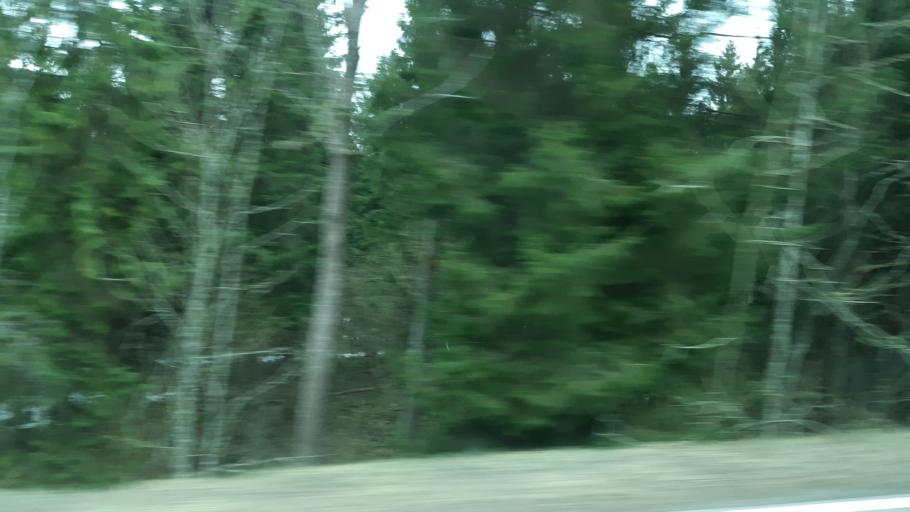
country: PL
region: Podlasie
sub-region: Suwalki
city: Suwalki
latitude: 54.3024
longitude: 22.9579
